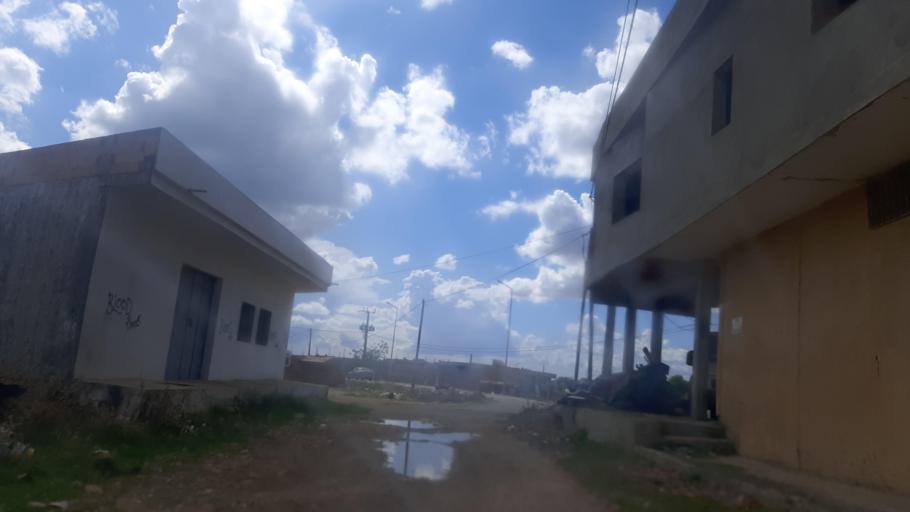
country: TN
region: Nabul
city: Korba
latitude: 36.5897
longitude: 10.8559
